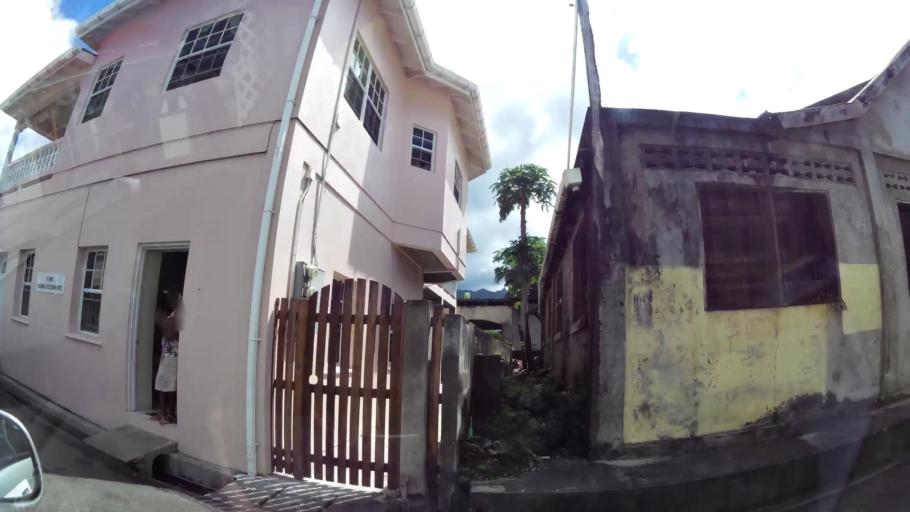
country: GD
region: Saint Mark
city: Victoria
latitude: 12.1959
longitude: -61.7054
